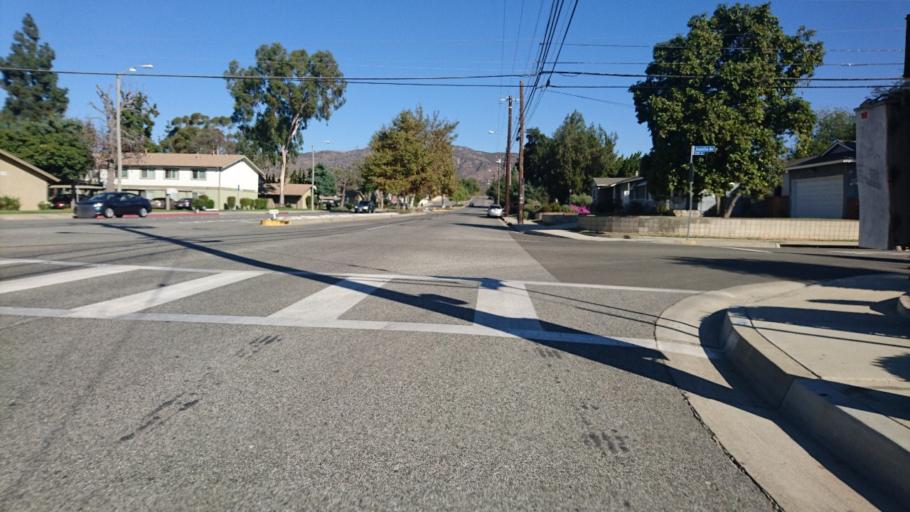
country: US
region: California
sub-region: Los Angeles County
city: San Dimas
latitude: 34.1101
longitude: -117.7939
